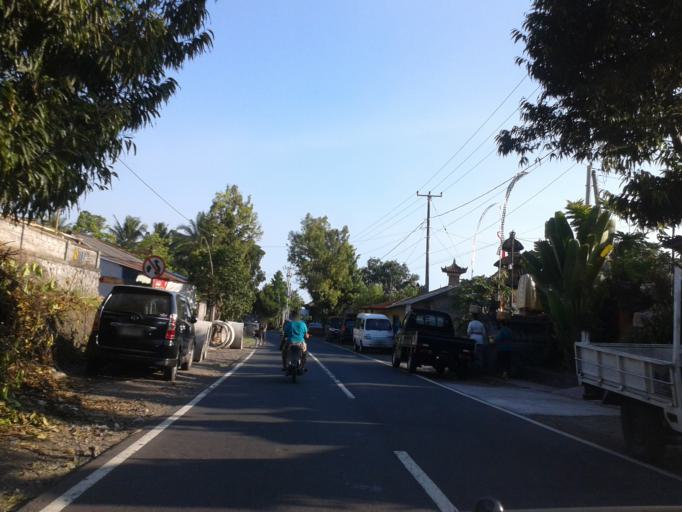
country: ID
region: Bali
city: Banjar Wangsian
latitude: -8.4997
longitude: 115.4035
